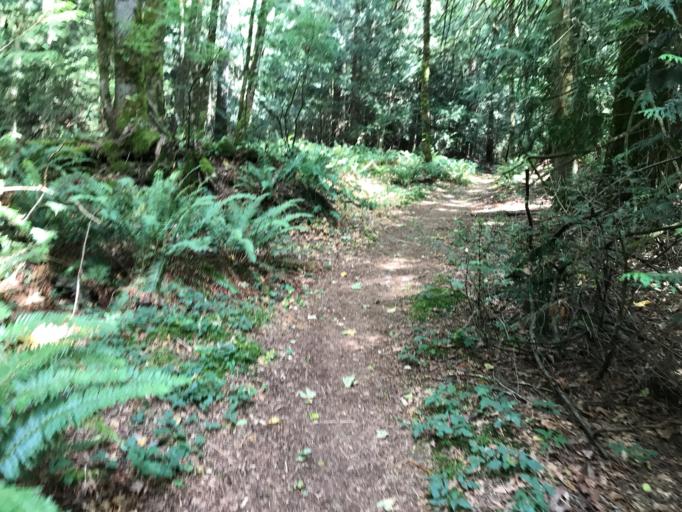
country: CA
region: British Columbia
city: North Cowichan
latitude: 48.9251
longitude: -123.7398
